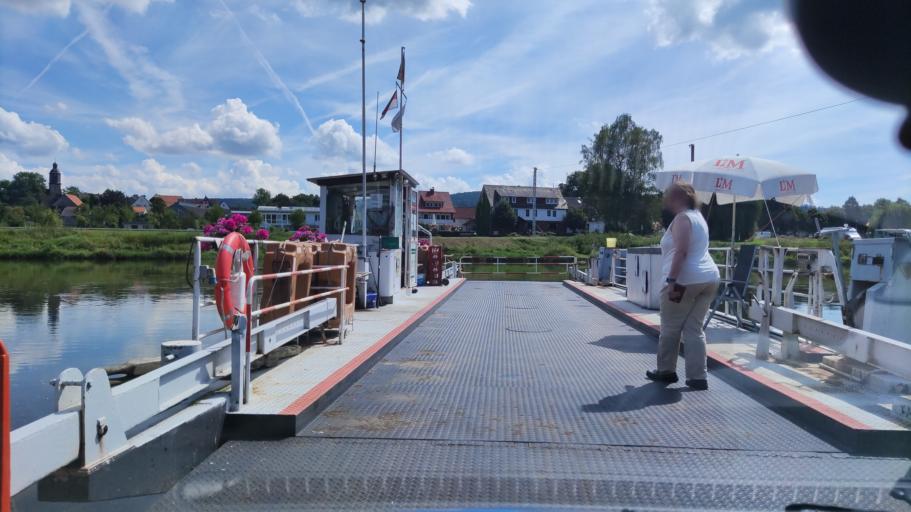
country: DE
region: Lower Saxony
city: Bodenfelde
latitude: 51.6258
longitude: 9.5507
